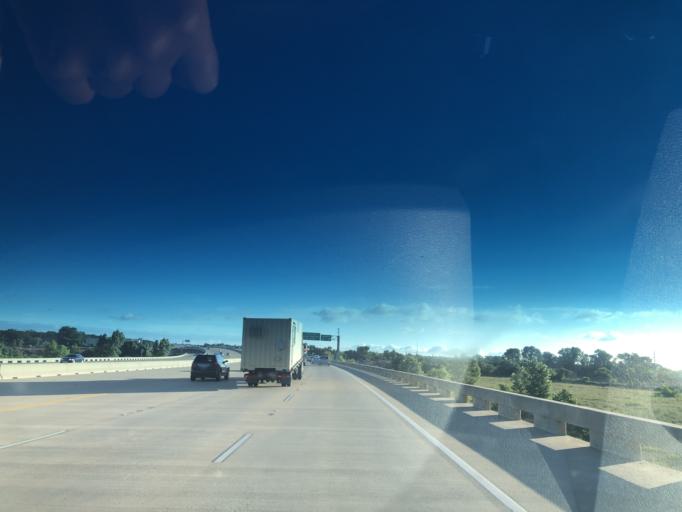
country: US
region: Texas
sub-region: Dallas County
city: Grand Prairie
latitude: 32.7870
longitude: -97.0193
